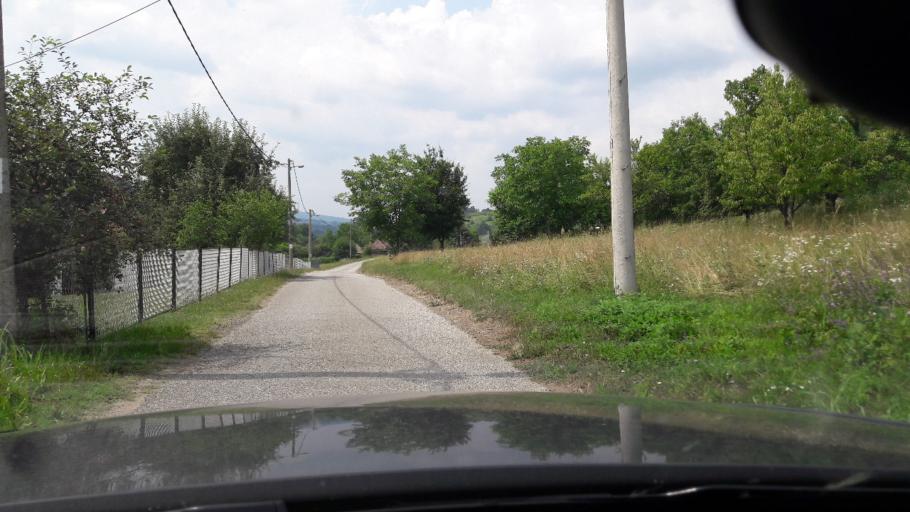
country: RS
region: Central Serbia
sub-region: Belgrade
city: Sopot
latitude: 44.6298
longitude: 20.5951
